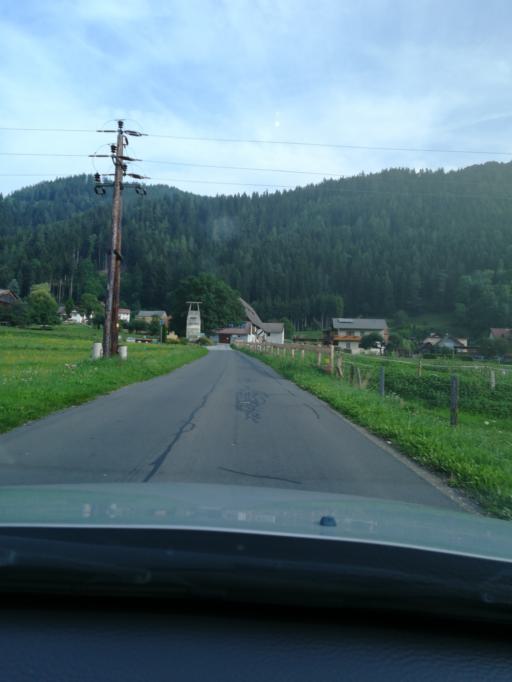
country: AT
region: Styria
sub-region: Politischer Bezirk Murtal
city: Sankt Georgen ob Judenburg
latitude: 47.2152
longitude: 14.4889
